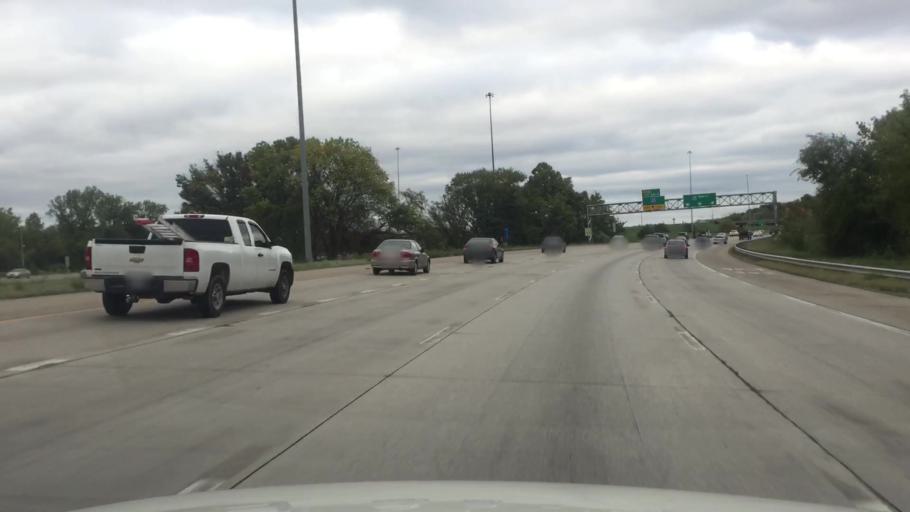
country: US
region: Kansas
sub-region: Johnson County
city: Merriam
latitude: 39.0383
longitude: -94.6800
